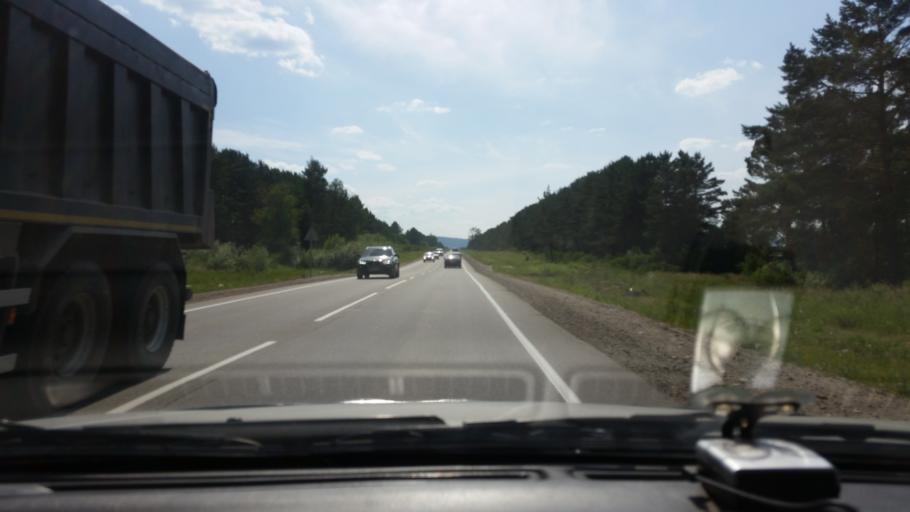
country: RU
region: Irkutsk
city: Baklashi
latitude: 52.1966
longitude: 104.0548
